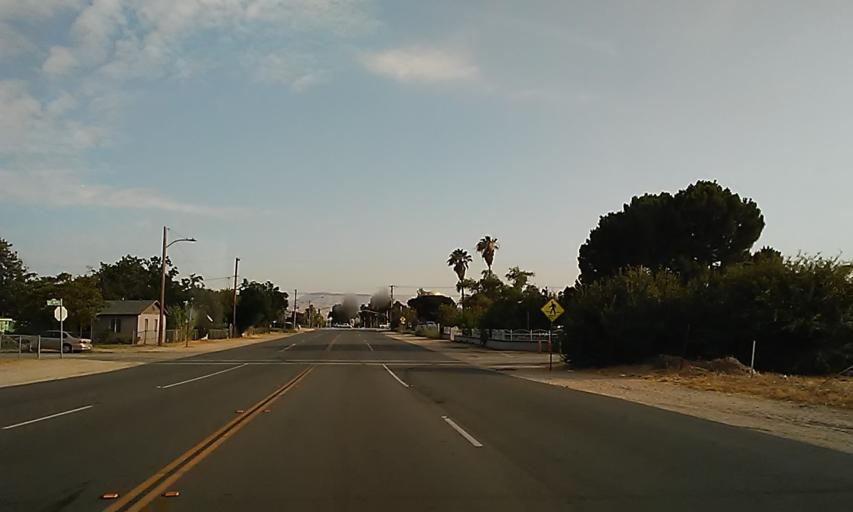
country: US
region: California
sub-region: San Bernardino County
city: San Bernardino
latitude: 34.1069
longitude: -117.2513
